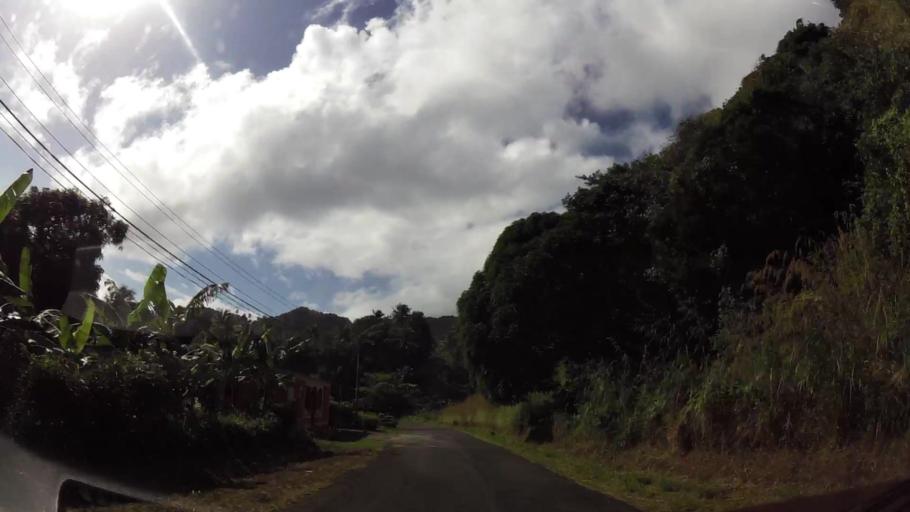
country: DM
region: Saint David
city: Castle Bruce
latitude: 15.4881
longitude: -61.2549
